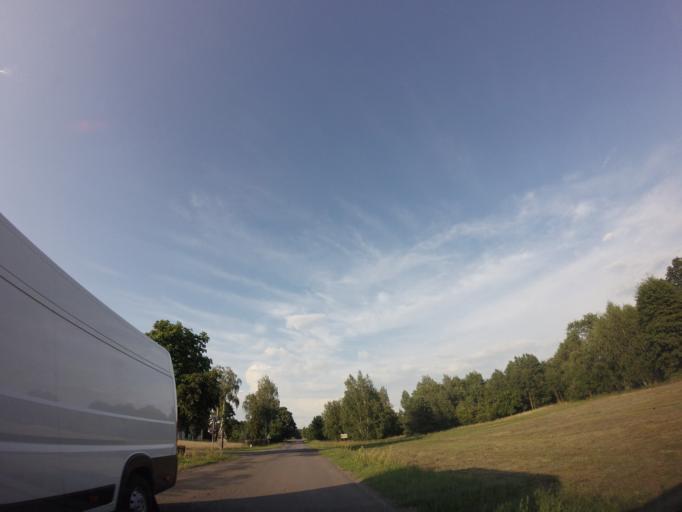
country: PL
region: Lublin Voivodeship
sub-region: Powiat pulawski
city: Kurow
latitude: 51.4247
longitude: 22.2050
